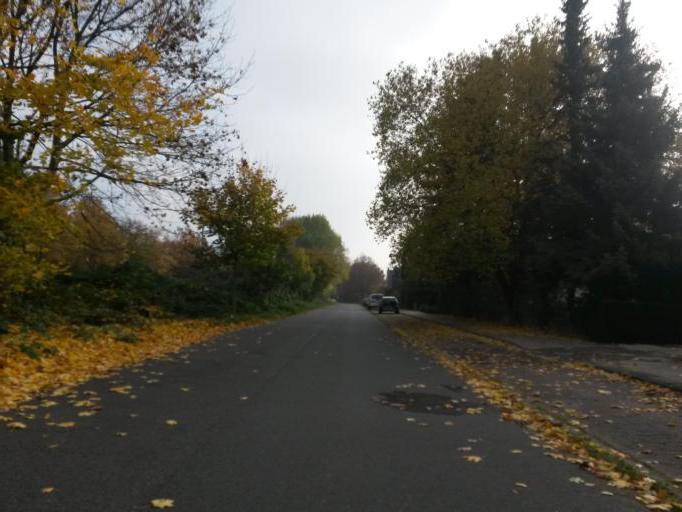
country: DE
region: Bremen
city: Bremen
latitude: 53.0802
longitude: 8.8581
